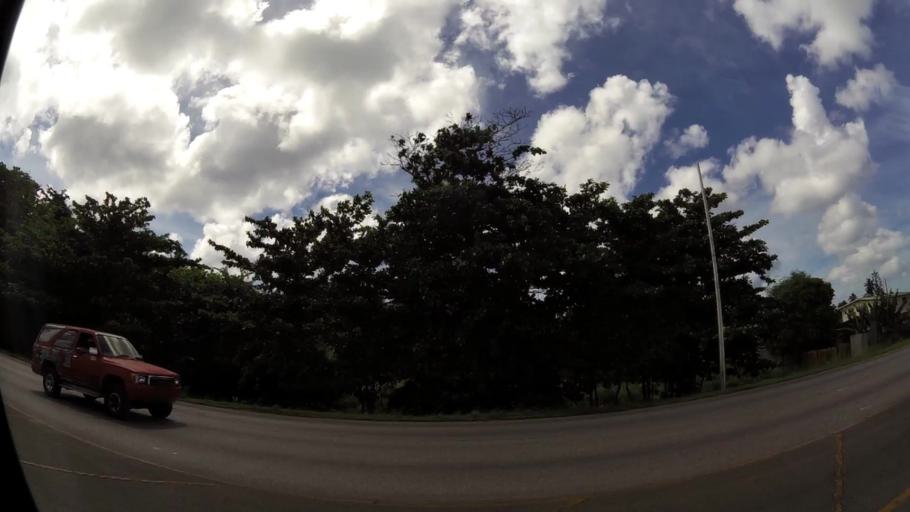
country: BB
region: Saint Michael
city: Bridgetown
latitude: 13.1204
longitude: -59.6273
